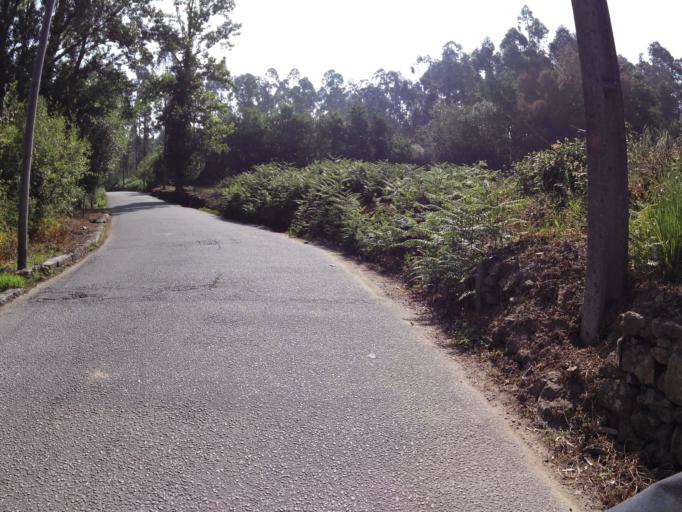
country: PT
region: Aveiro
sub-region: Santa Maria da Feira
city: Argoncilhe
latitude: 41.0369
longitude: -8.5412
